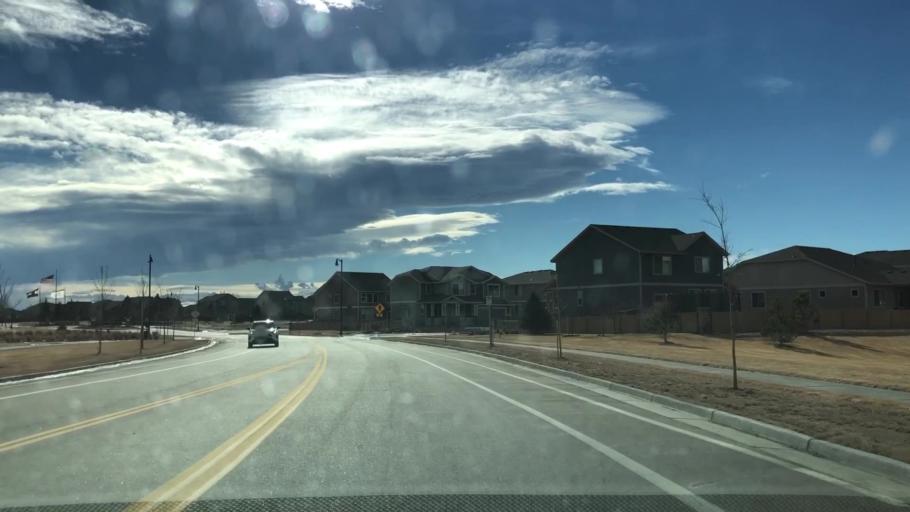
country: US
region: Colorado
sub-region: Weld County
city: Windsor
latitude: 40.5106
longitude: -104.9540
